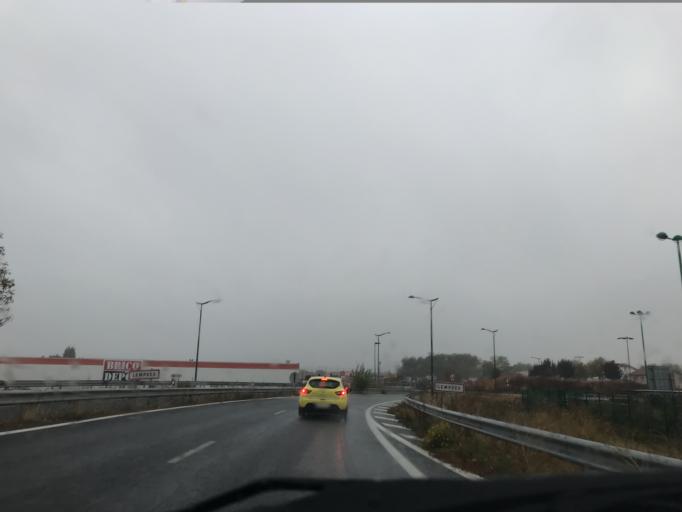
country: FR
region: Auvergne
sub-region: Departement du Puy-de-Dome
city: Aulnat
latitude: 45.7773
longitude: 3.1864
